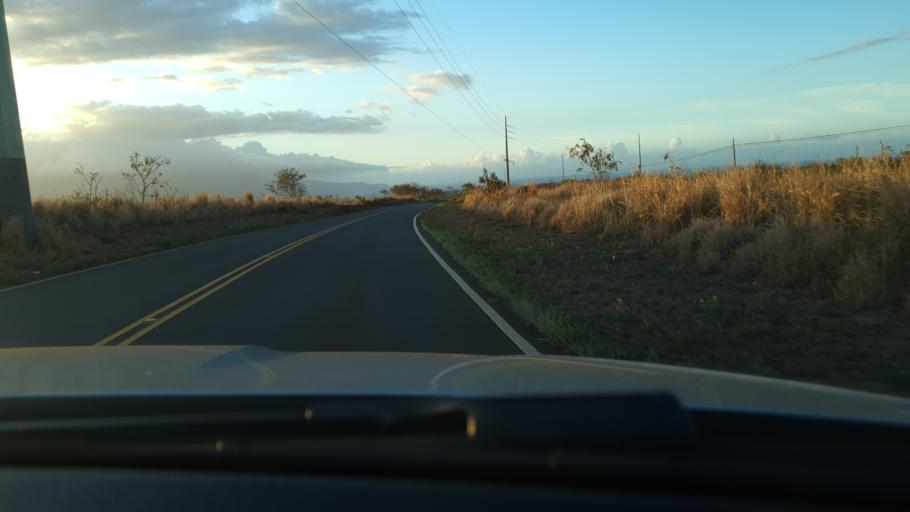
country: US
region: Hawaii
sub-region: Maui County
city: Pukalani
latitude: 20.8163
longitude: -156.3863
